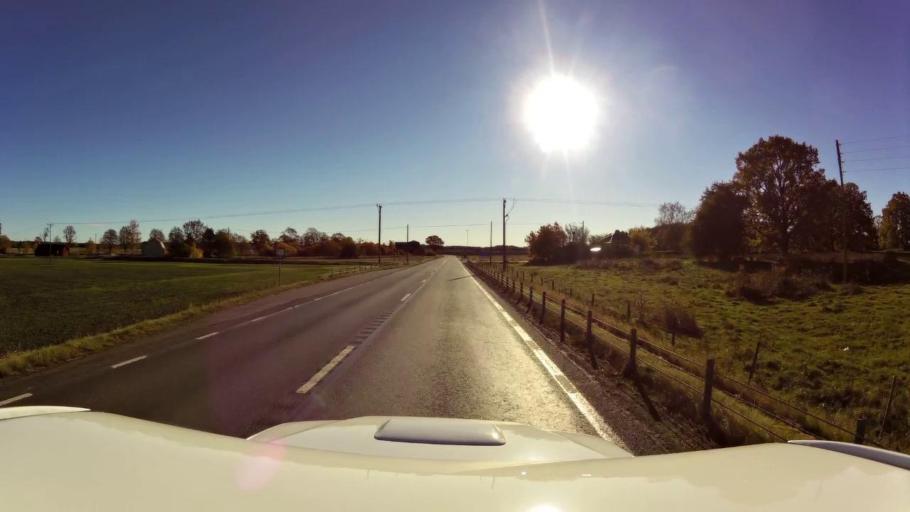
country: SE
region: OEstergoetland
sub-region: Linkopings Kommun
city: Ljungsbro
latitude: 58.5210
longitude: 15.4227
